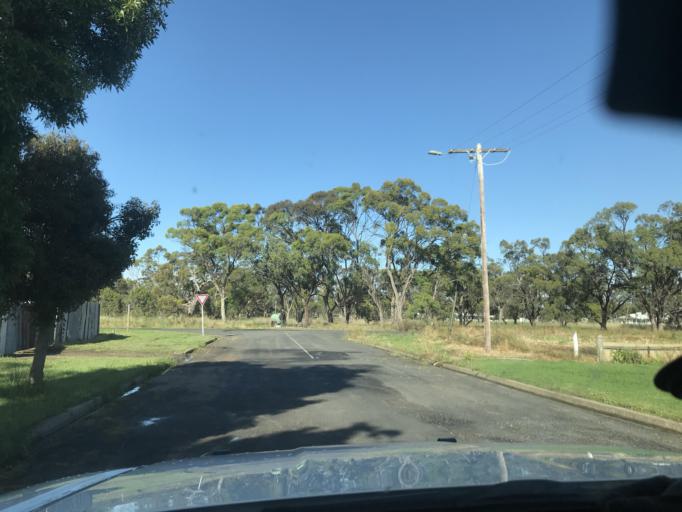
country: AU
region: Victoria
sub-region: Horsham
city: Horsham
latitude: -36.7215
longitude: 141.4717
